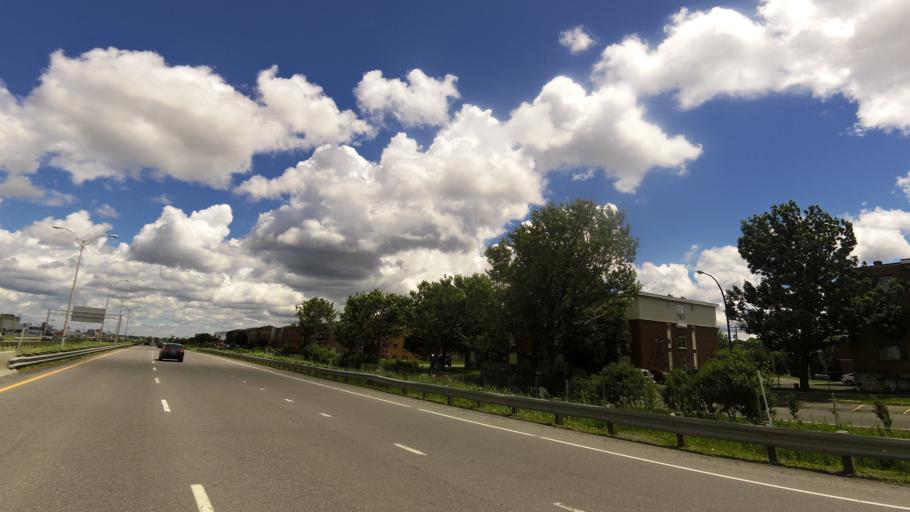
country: CA
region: Quebec
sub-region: Laurentides
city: Saint-Eustache
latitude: 45.5721
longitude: -73.9026
